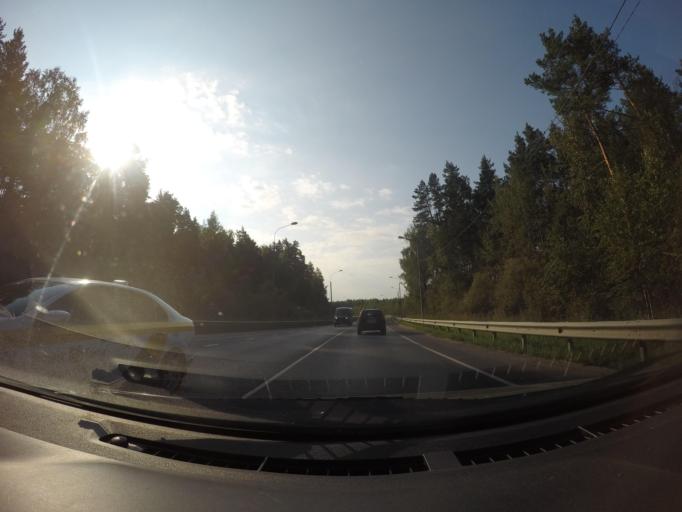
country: RU
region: Moskovskaya
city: Ramenskoye
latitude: 55.6327
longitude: 38.2779
